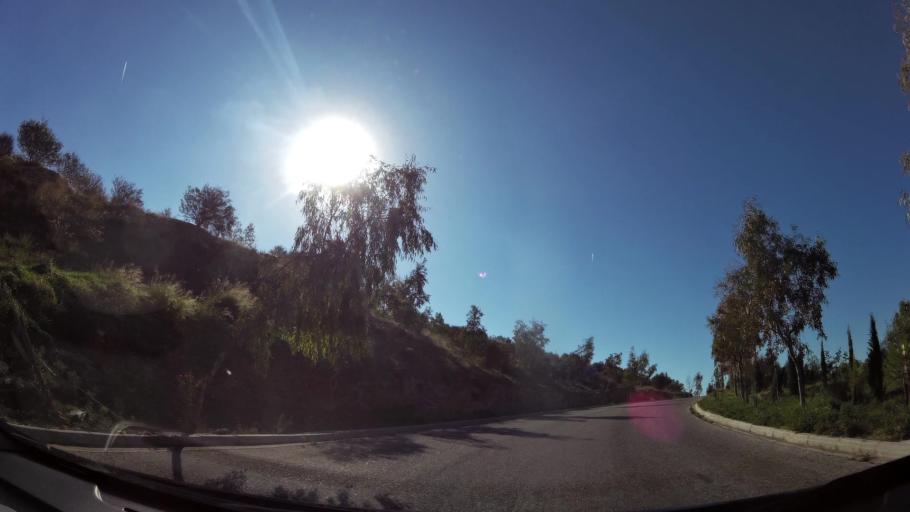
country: GR
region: Attica
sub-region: Nomarchia Athinas
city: Glyfada
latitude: 37.8650
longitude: 23.7724
